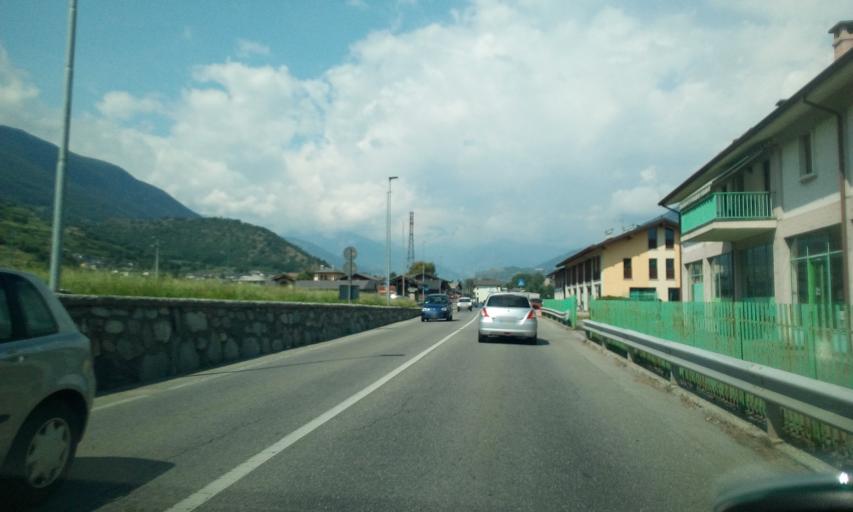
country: IT
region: Aosta Valley
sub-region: Valle d'Aosta
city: Aosta
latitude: 45.7269
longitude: 7.3110
